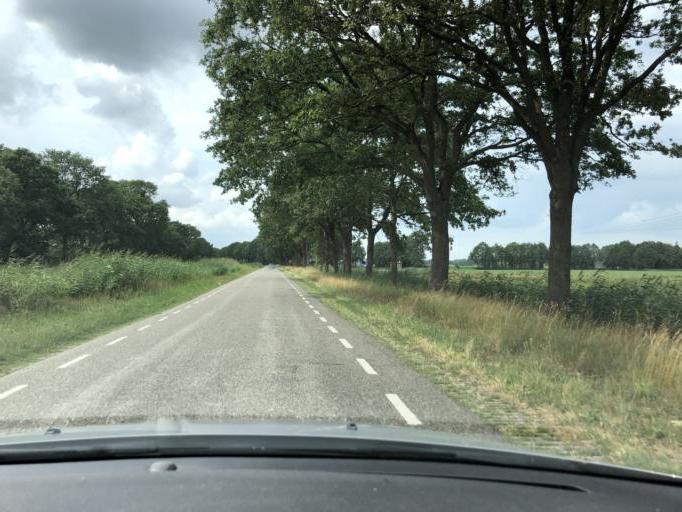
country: NL
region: Drenthe
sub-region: Gemeente Borger-Odoorn
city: Borger
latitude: 52.8598
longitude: 6.6535
